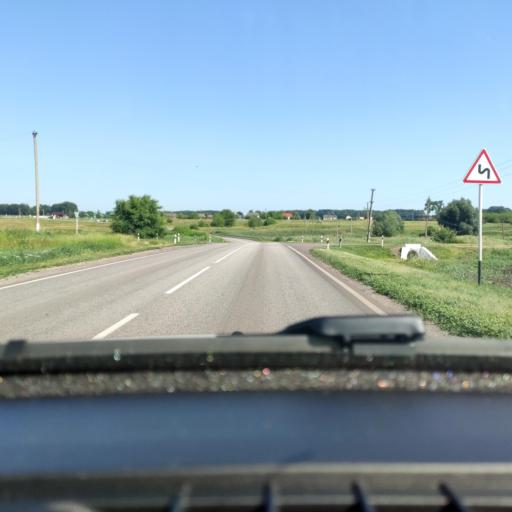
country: RU
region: Voronezj
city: Panino
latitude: 51.6517
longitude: 40.0121
